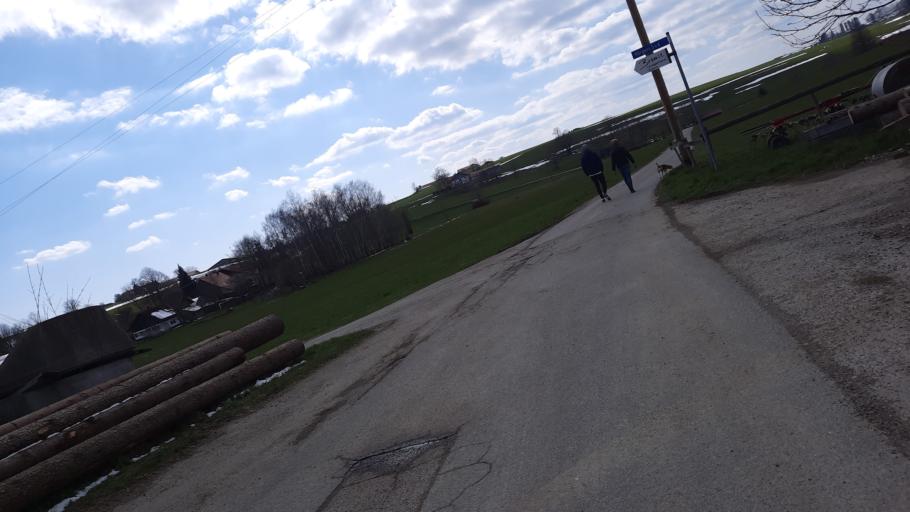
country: DE
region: Bavaria
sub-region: Swabia
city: Altusried
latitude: 47.8170
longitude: 10.2120
